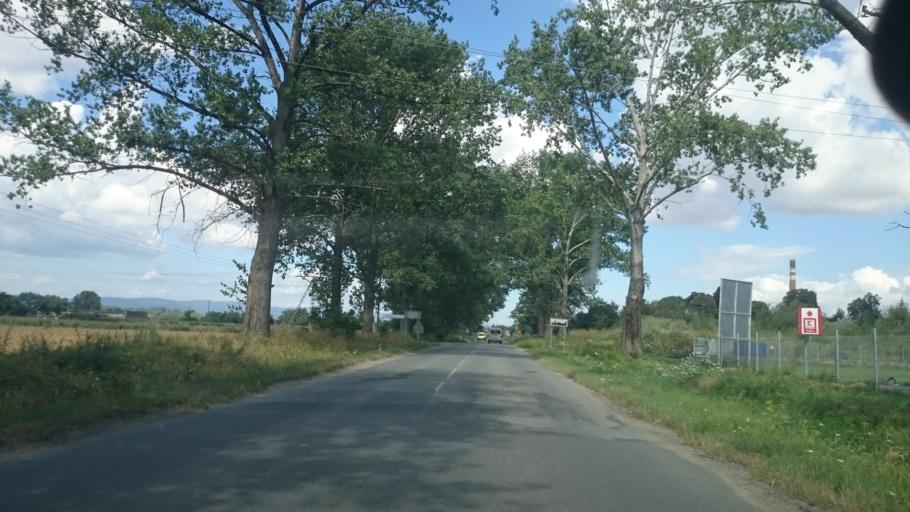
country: PL
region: Lower Silesian Voivodeship
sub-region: Powiat zabkowicki
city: Zabkowice Slaskie
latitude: 50.5778
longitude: 16.8342
